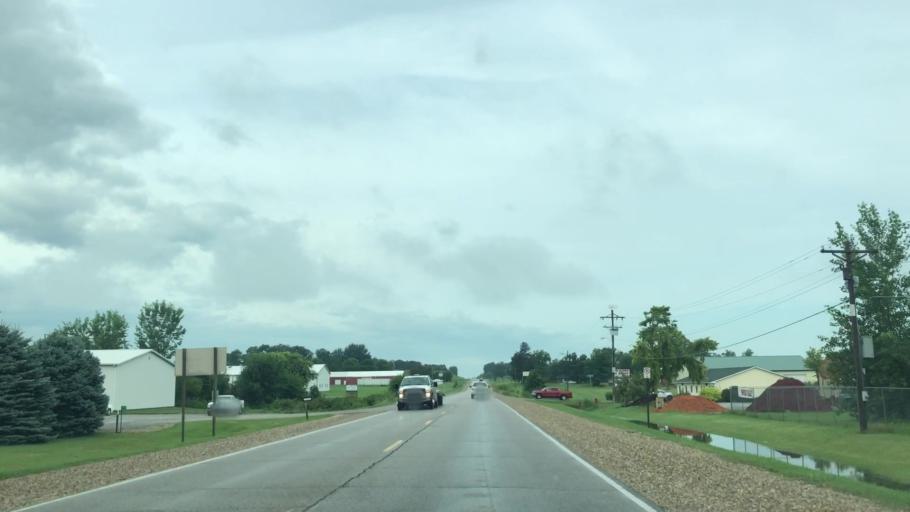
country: US
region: Iowa
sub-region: Marshall County
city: Marshalltown
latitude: 42.0074
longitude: -92.9350
